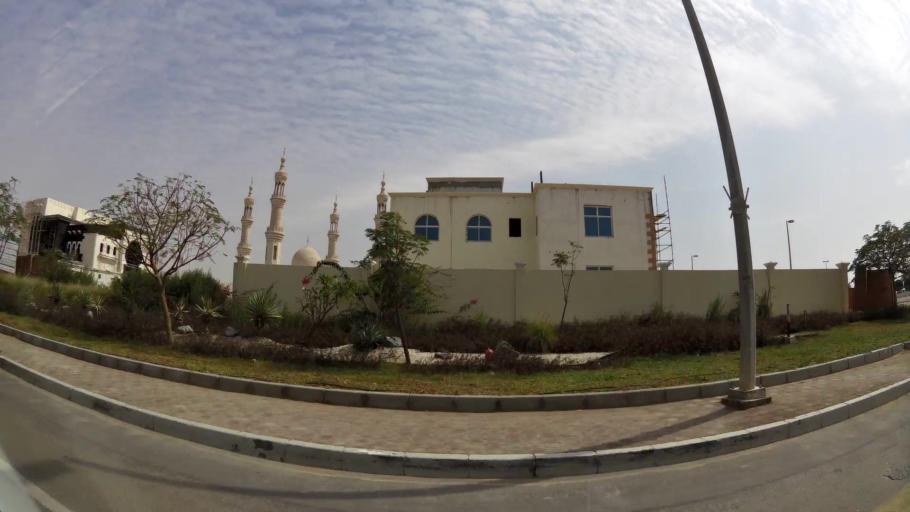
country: AE
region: Abu Dhabi
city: Abu Dhabi
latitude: 24.5160
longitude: 54.6633
